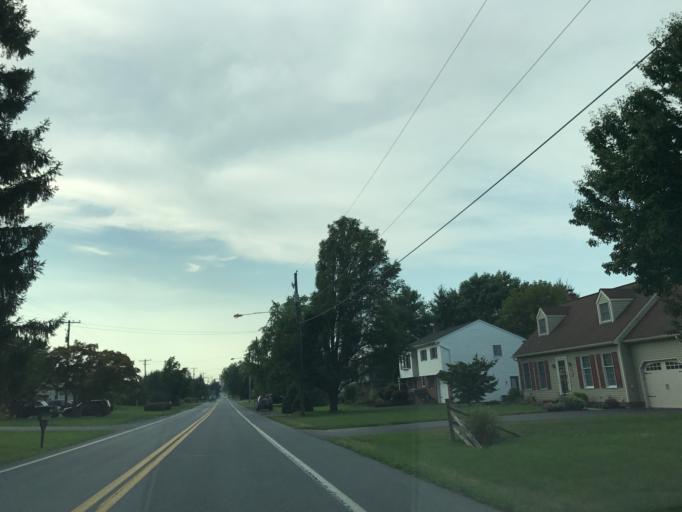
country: US
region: Pennsylvania
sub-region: Lancaster County
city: Rheems
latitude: 40.1266
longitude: -76.5591
